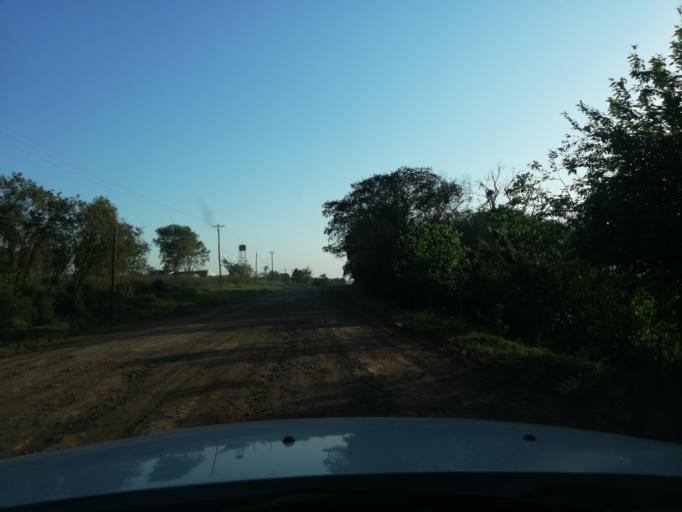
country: AR
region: Misiones
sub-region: Departamento de Apostoles
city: San Jose
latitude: -27.6319
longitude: -55.7295
